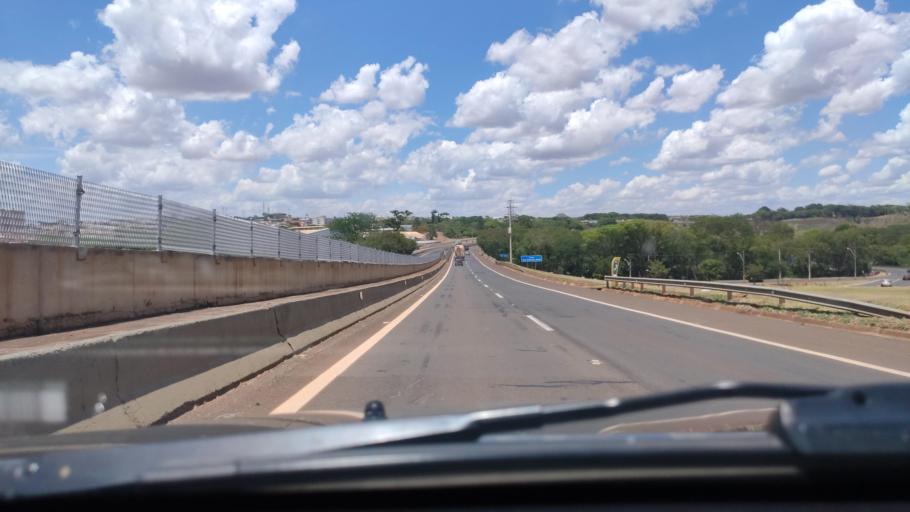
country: BR
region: Sao Paulo
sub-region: Jau
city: Jau
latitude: -22.2773
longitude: -48.5657
